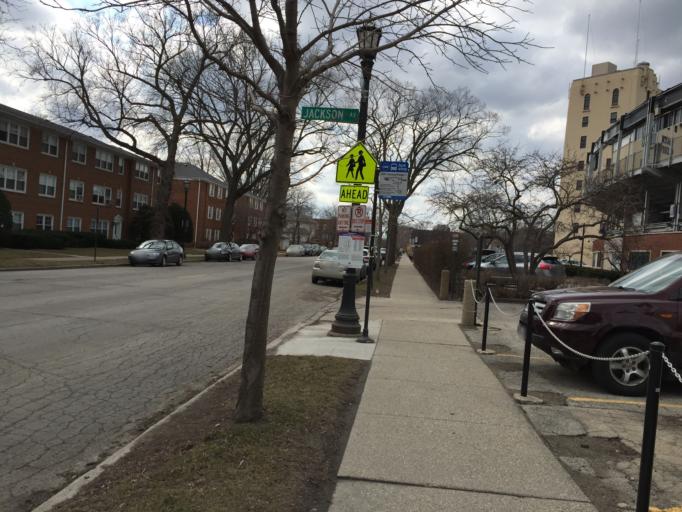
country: US
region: Illinois
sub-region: Cook County
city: Evanston
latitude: 42.0643
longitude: -87.6920
